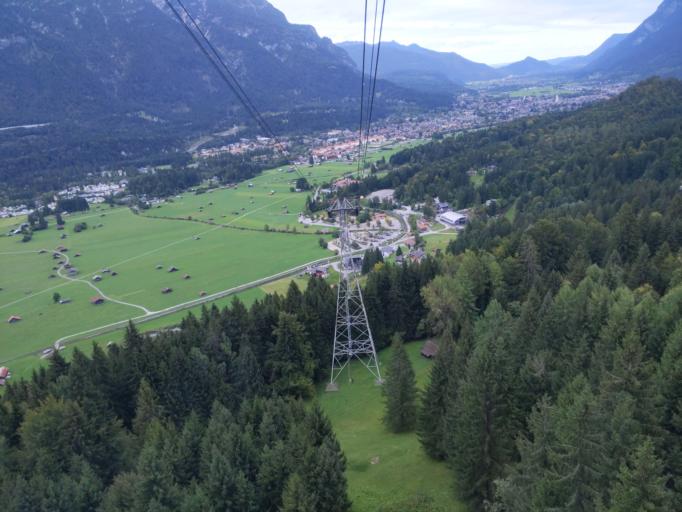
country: DE
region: Bavaria
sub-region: Upper Bavaria
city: Grainau
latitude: 47.4649
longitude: 11.0595
